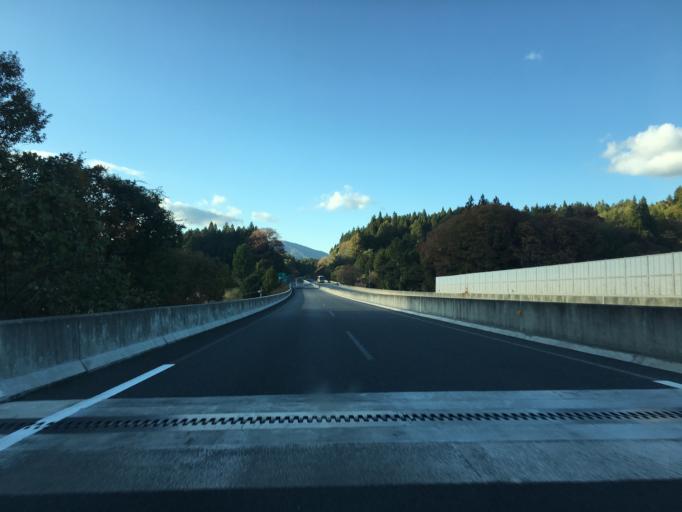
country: JP
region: Fukushima
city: Funehikimachi-funehiki
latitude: 37.2789
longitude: 140.6204
